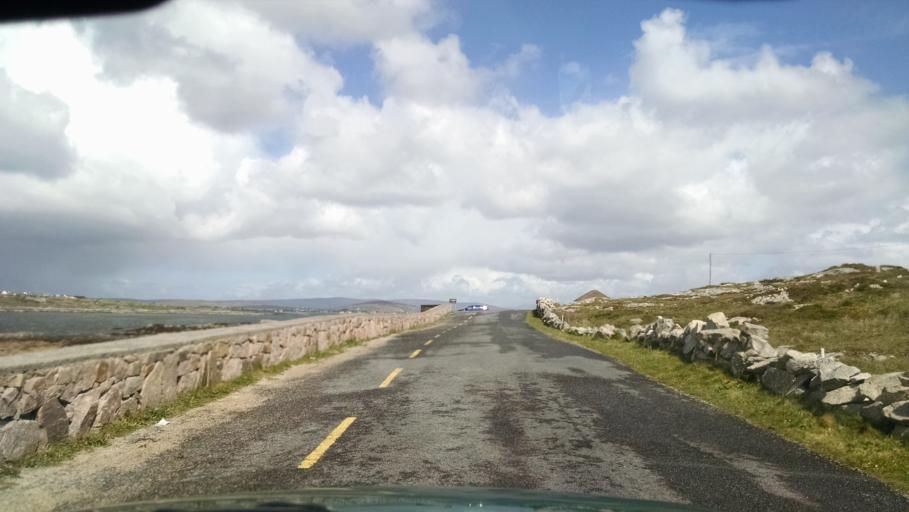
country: IE
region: Connaught
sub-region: County Galway
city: Oughterard
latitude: 53.2479
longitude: -9.6288
